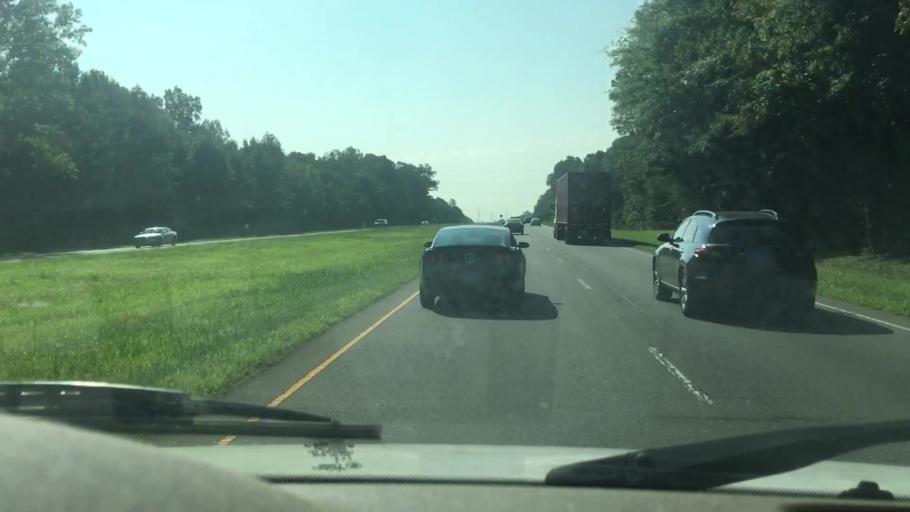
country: US
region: North Carolina
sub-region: Gaston County
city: Mount Holly
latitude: 35.3349
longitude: -80.9586
